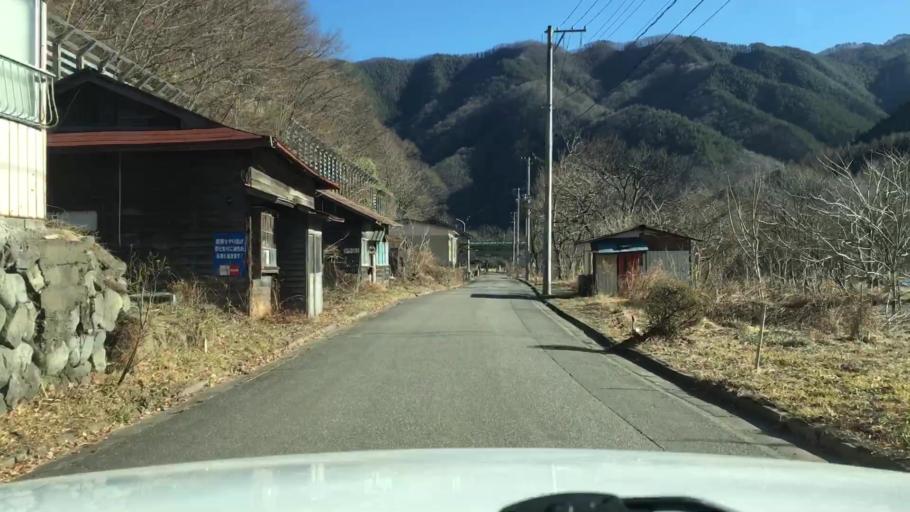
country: JP
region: Iwate
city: Miyako
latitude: 39.6217
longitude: 141.8012
